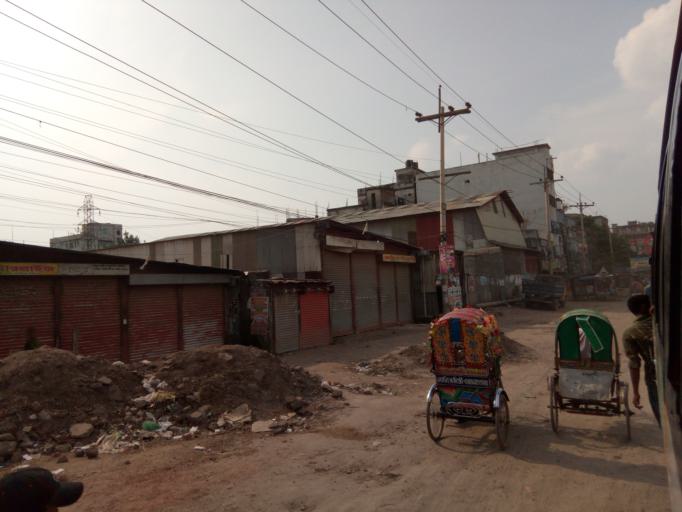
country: BD
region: Dhaka
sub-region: Dhaka
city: Dhaka
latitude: 23.6965
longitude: 90.3984
